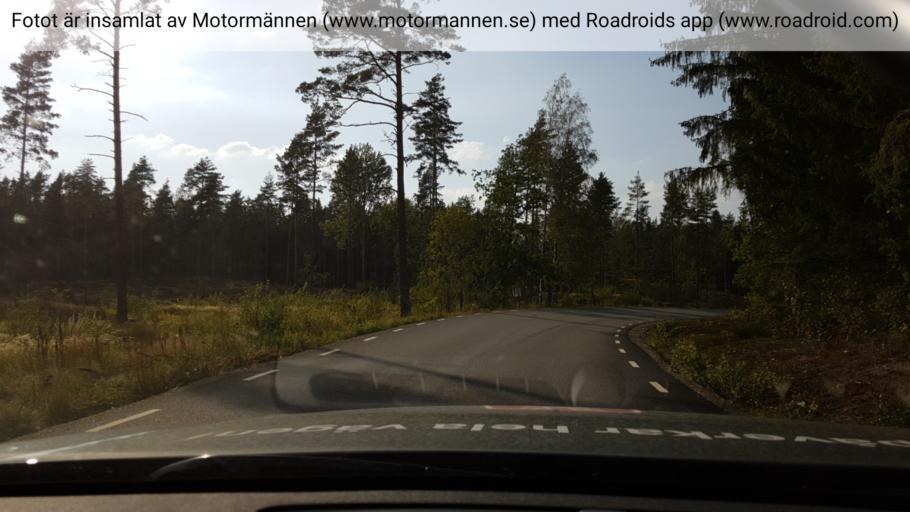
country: SE
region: Soedermanland
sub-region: Gnesta Kommun
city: Gnesta
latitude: 59.1186
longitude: 17.2181
